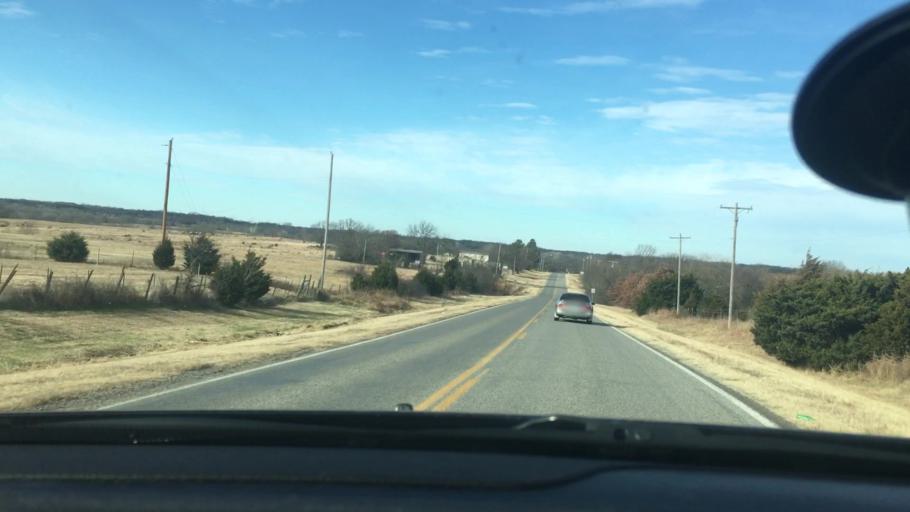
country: US
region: Oklahoma
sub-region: Seminole County
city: Konawa
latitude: 34.9492
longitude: -96.7415
